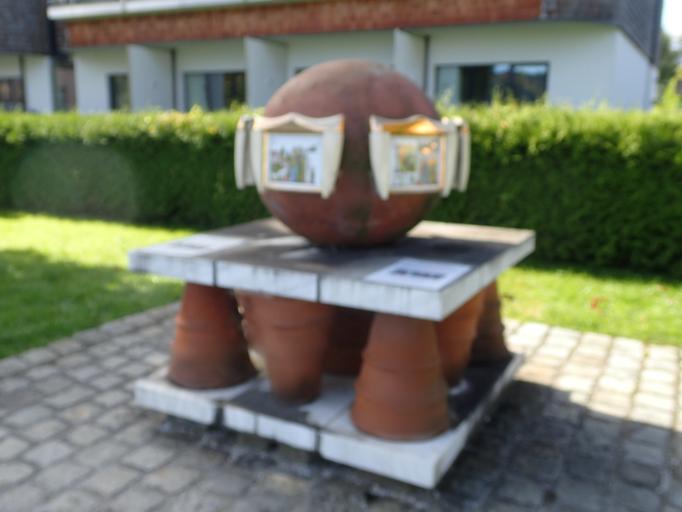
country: AT
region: Salzburg
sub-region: Politischer Bezirk Salzburg-Umgebung
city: Mattsee
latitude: 47.9720
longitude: 13.1059
